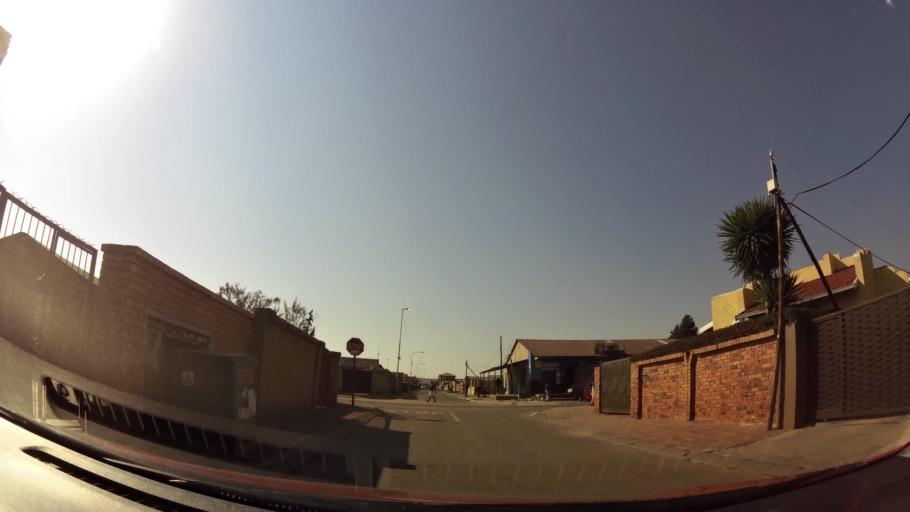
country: ZA
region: Gauteng
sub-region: City of Johannesburg Metropolitan Municipality
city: Soweto
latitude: -26.2439
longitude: 27.9447
